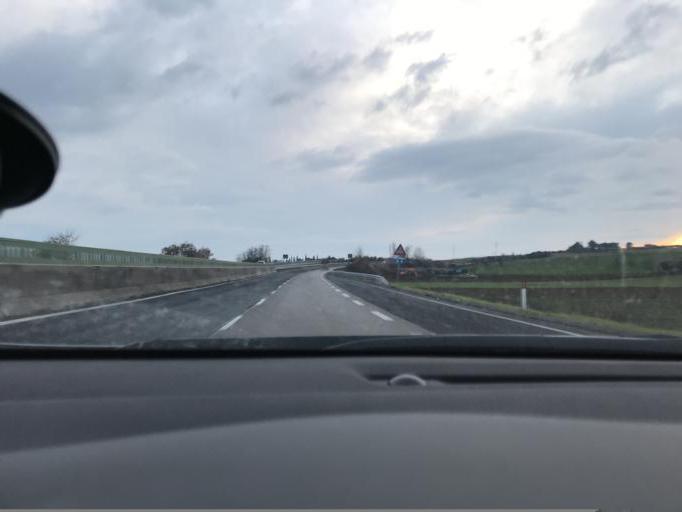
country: IT
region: Umbria
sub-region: Provincia di Perugia
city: Petrignano
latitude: 43.1140
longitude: 12.5076
